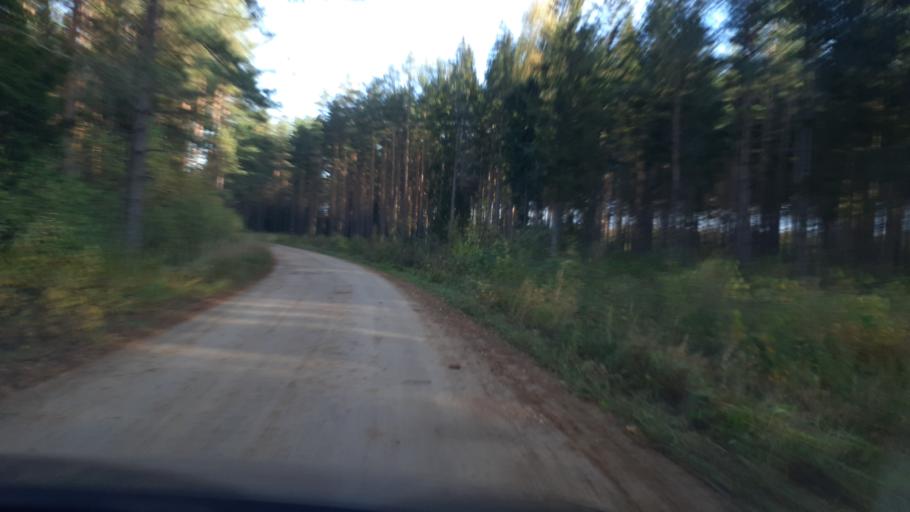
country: LV
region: Kuldigas Rajons
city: Kuldiga
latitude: 56.8569
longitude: 22.1055
